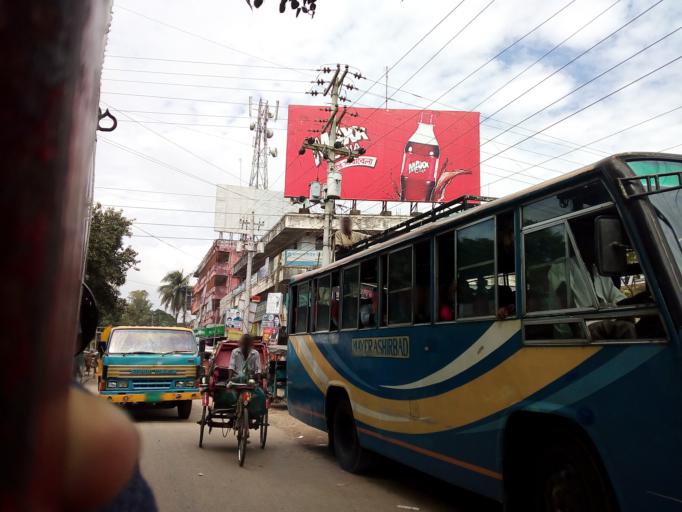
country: BD
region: Rangpur Division
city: Nageswari
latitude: 25.9657
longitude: 89.6914
